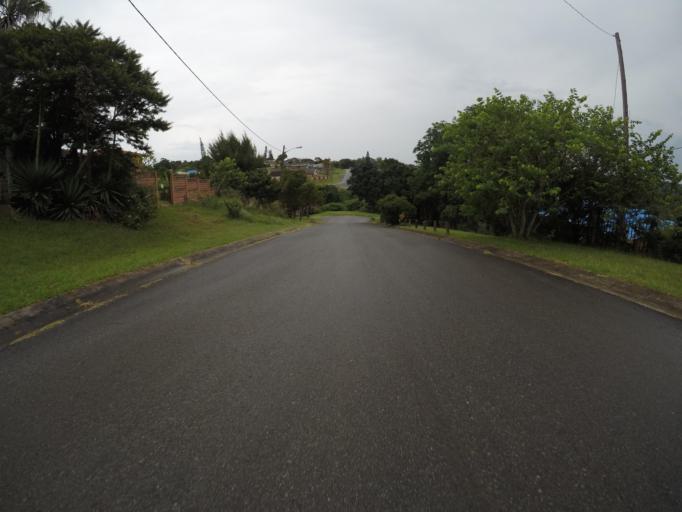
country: ZA
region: Eastern Cape
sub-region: Buffalo City Metropolitan Municipality
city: East London
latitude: -32.9635
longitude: 27.8484
